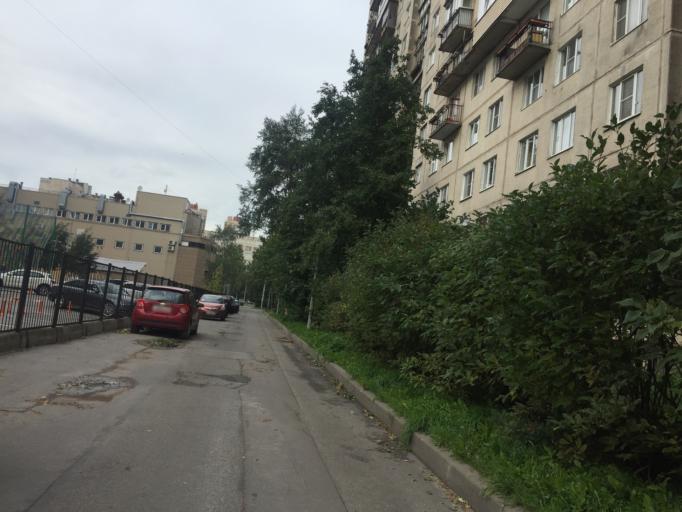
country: RU
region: St.-Petersburg
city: Shushary
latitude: 59.8300
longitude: 30.3869
